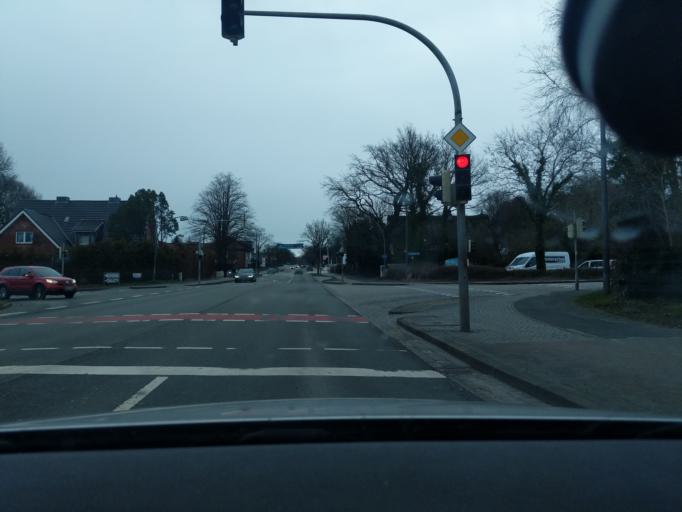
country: DE
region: Lower Saxony
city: Stade
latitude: 53.5957
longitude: 9.4385
